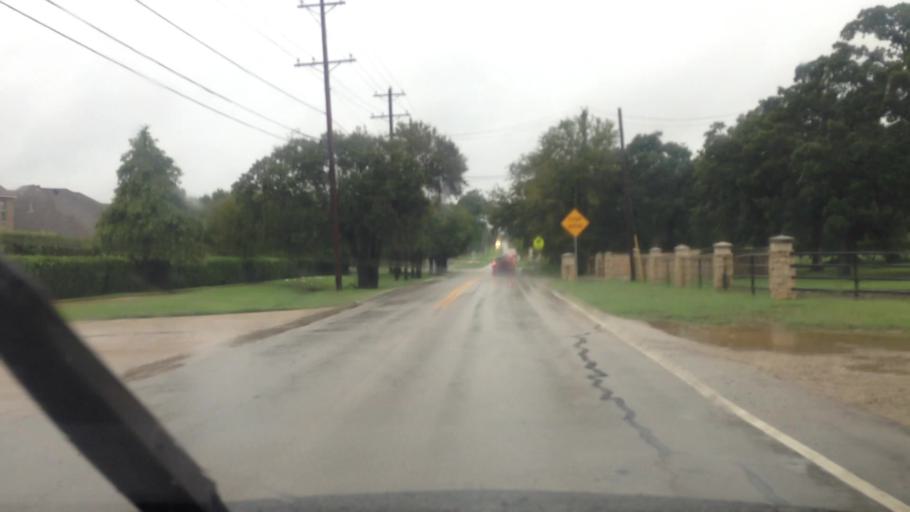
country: US
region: Texas
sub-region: Tarrant County
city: Keller
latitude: 32.9076
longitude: -97.2210
